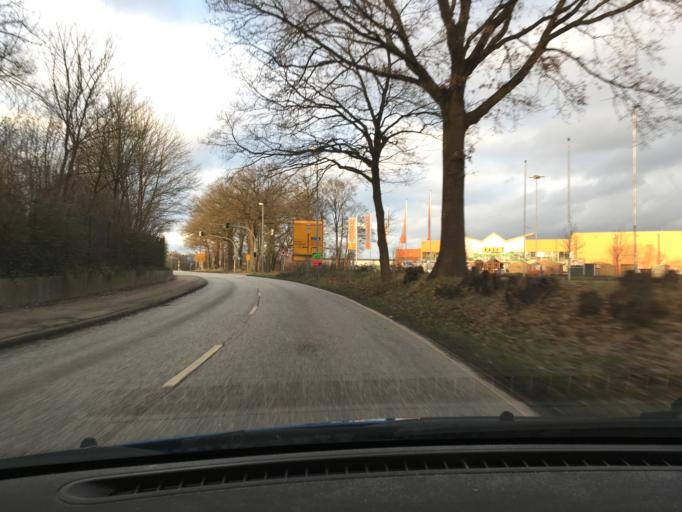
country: DE
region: Schleswig-Holstein
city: Kolln-Reisiek
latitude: 53.7423
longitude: 9.7070
